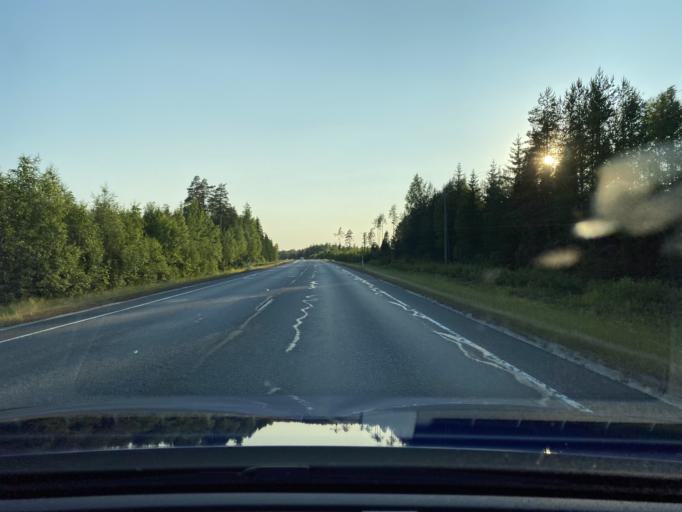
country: FI
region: Haeme
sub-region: Forssa
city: Tammela
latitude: 60.8296
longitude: 23.8764
